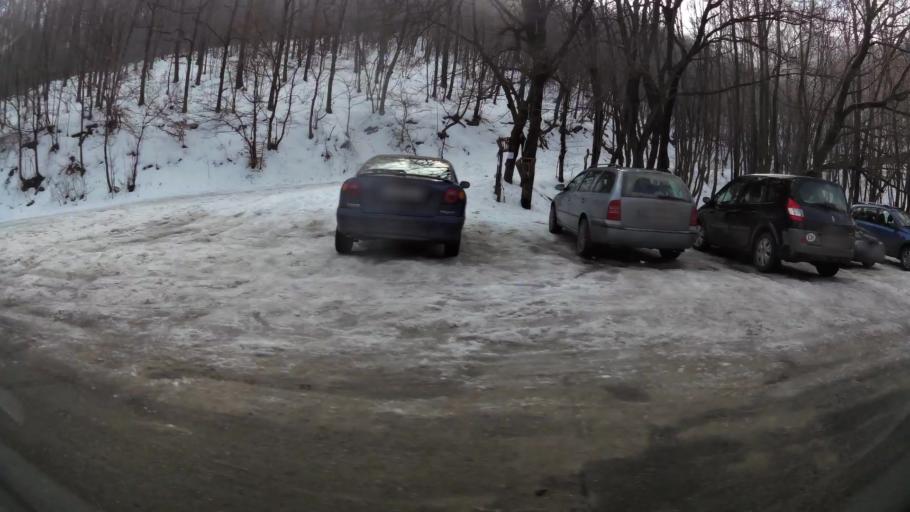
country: BG
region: Sofia-Capital
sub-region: Stolichna Obshtina
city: Sofia
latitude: 42.6431
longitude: 23.2326
